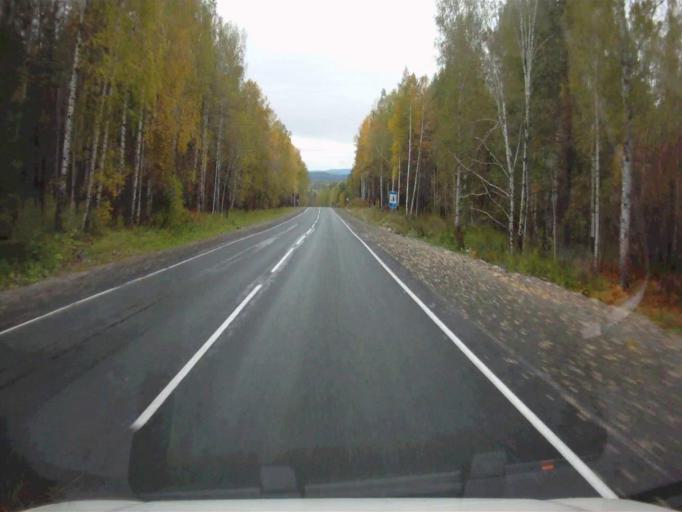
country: RU
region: Chelyabinsk
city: Nyazepetrovsk
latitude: 56.0531
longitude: 59.7407
